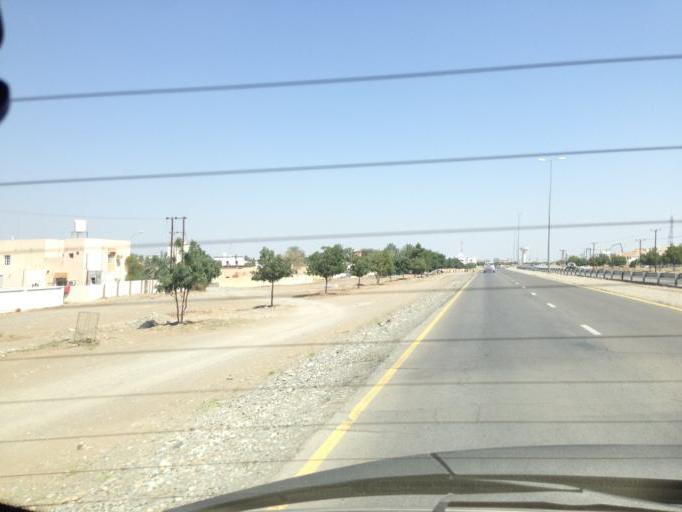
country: OM
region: Al Batinah
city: Rustaq
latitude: 23.5343
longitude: 57.4684
